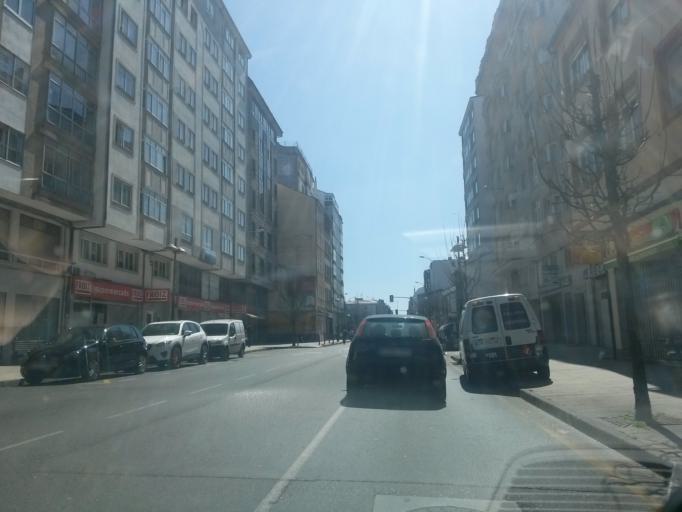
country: ES
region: Galicia
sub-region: Provincia de Lugo
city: Lugo
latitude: 43.0234
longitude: -7.5656
